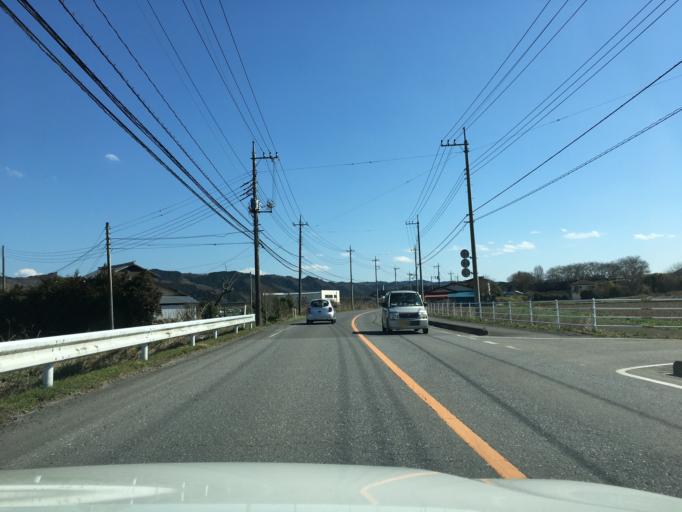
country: JP
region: Tochigi
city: Karasuyama
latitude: 36.7247
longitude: 140.1447
